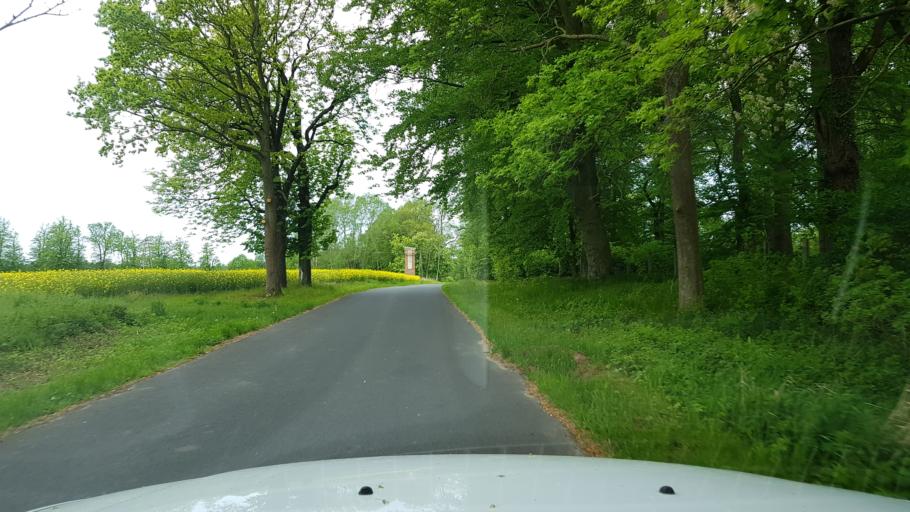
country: PL
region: West Pomeranian Voivodeship
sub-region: Powiat kolobrzeski
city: Ustronie Morskie
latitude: 54.2220
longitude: 15.8024
